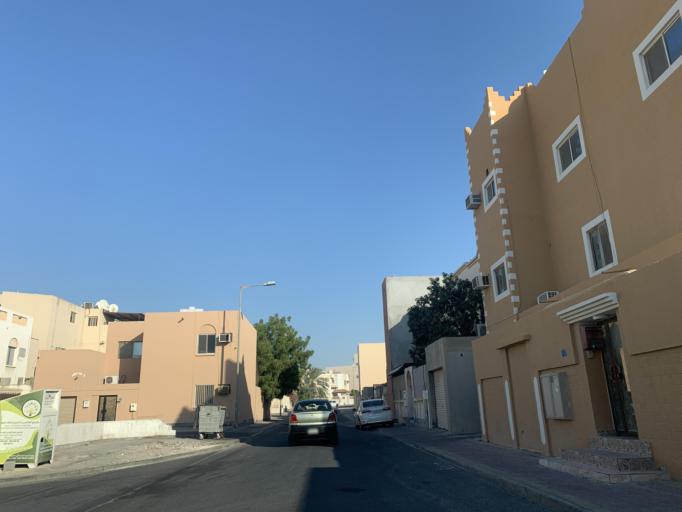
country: BH
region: Central Governorate
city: Madinat Hamad
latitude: 26.1103
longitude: 50.5057
